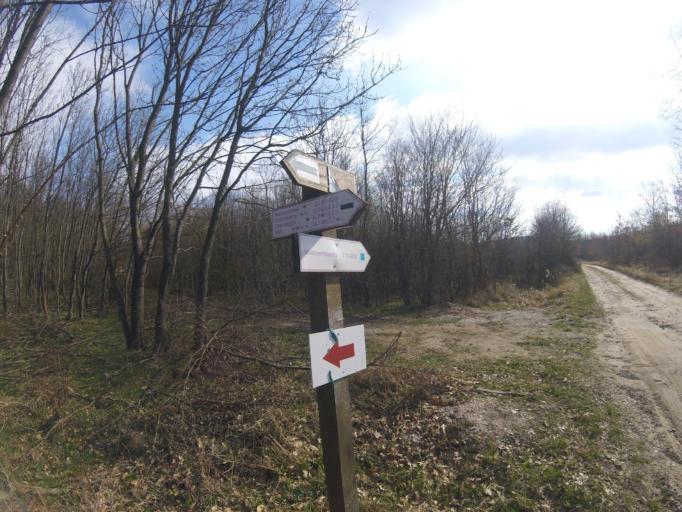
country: HU
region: Komarom-Esztergom
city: Oroszlany
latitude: 47.4230
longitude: 18.3148
